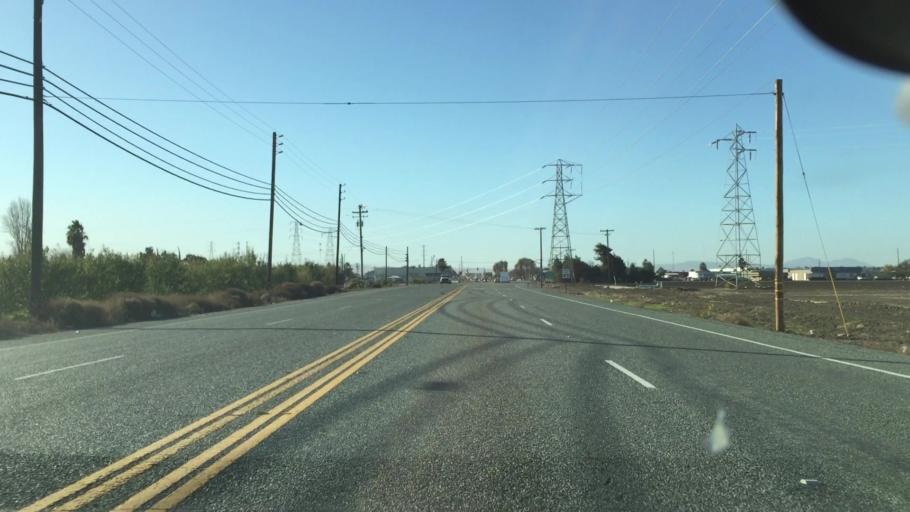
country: US
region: California
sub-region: San Joaquin County
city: Tracy
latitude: 37.7397
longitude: -121.3925
